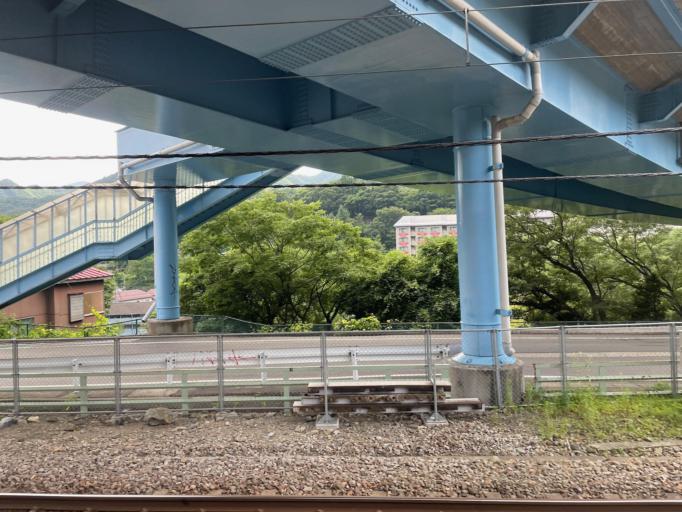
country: JP
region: Gunma
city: Numata
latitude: 36.7755
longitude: 138.9697
